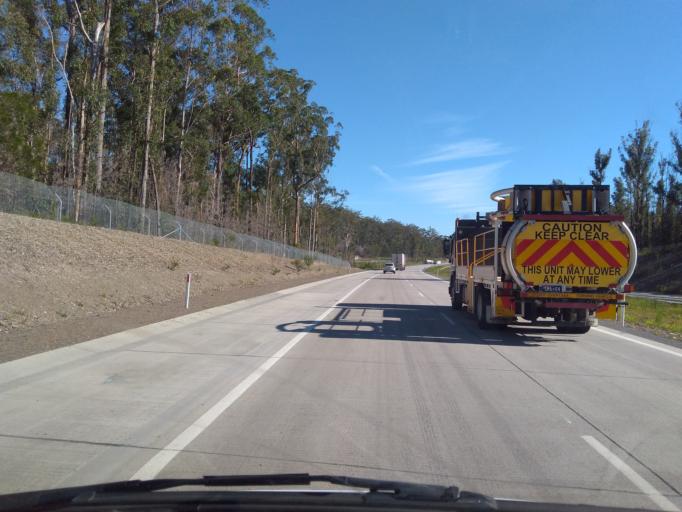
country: AU
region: New South Wales
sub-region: Kempsey
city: Kempsey
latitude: -31.1491
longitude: 152.8207
